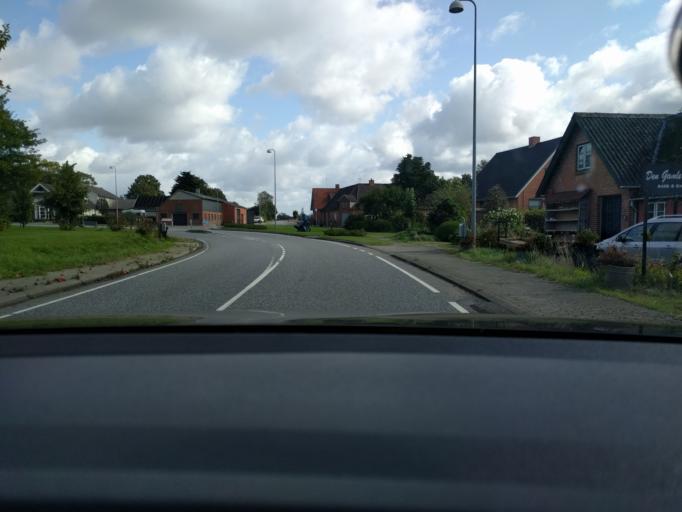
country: DK
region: Central Jutland
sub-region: Viborg Kommune
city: Bjerringbro
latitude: 56.3047
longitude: 9.7151
